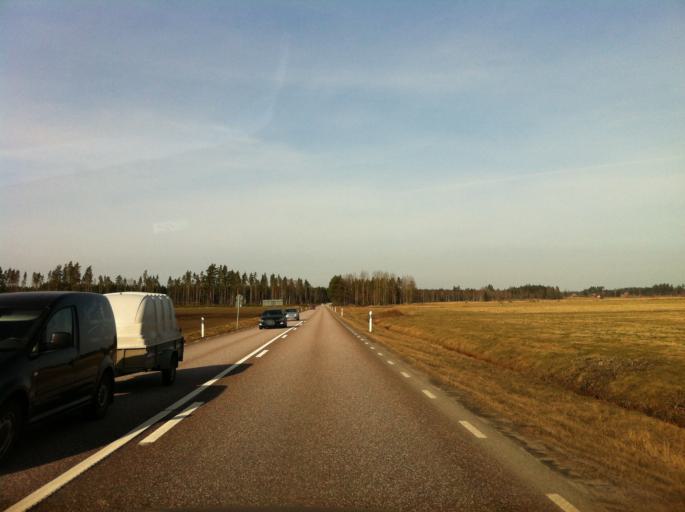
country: SE
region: Vaestra Goetaland
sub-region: Skovde Kommun
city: Skultorp
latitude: 58.2561
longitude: 13.8127
